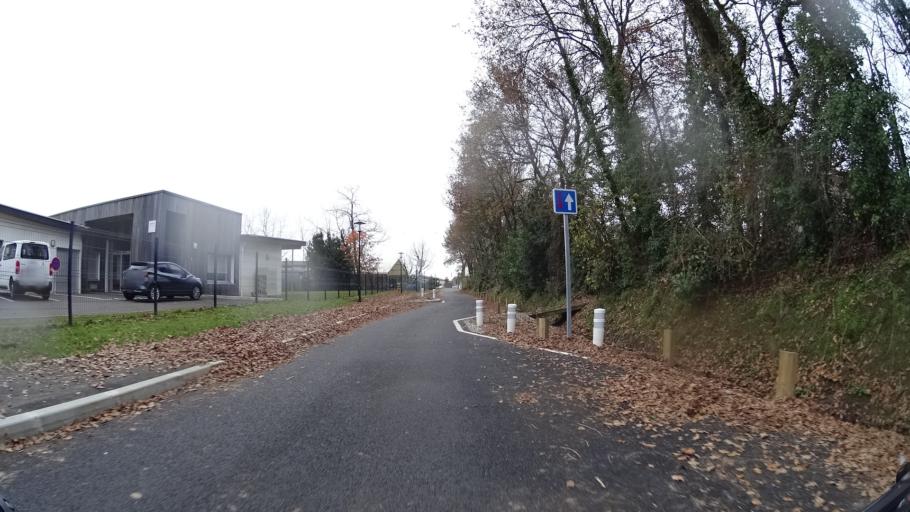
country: FR
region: Aquitaine
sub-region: Departement des Landes
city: Saint-Paul-les-Dax
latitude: 43.7346
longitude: -1.0526
